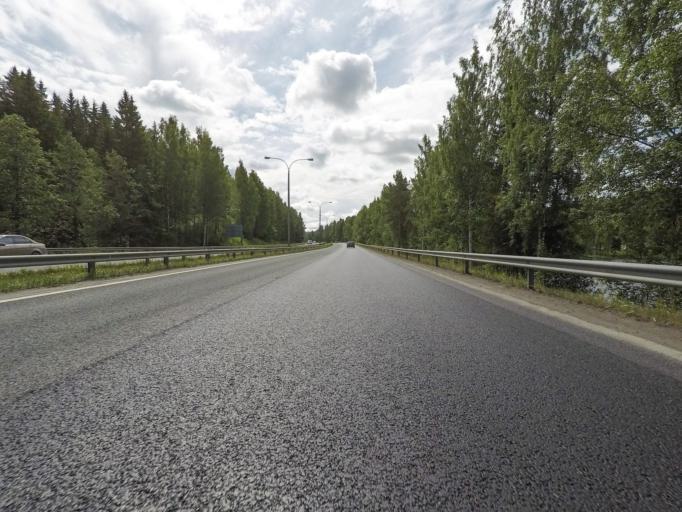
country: FI
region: Northern Savo
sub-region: Kuopio
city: Kuopio
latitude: 62.9264
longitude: 27.6753
